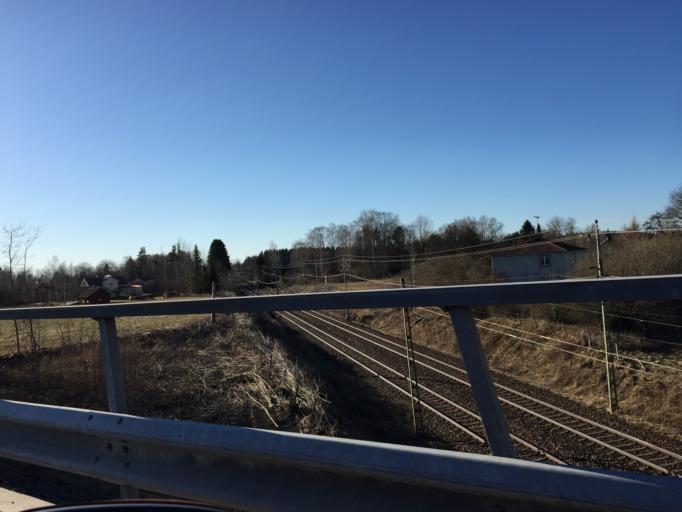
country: SE
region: Soedermanland
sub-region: Vingakers Kommun
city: Vingaker
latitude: 59.0468
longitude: 15.7892
